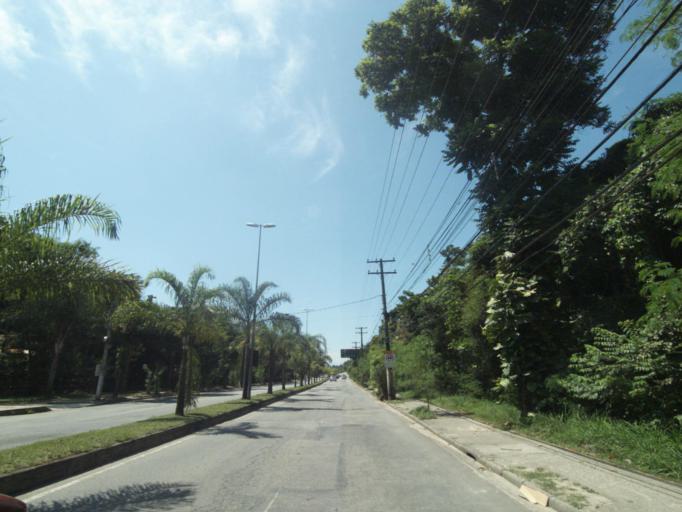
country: BR
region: Rio de Janeiro
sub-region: Niteroi
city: Niteroi
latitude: -22.8933
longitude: -43.0367
